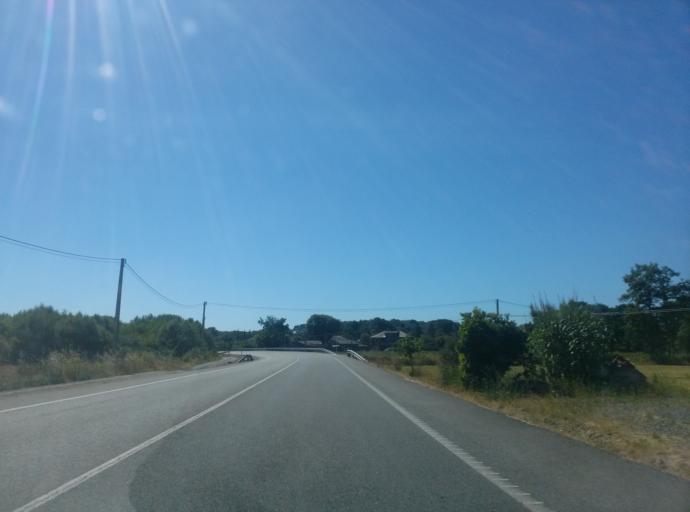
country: ES
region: Galicia
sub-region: Provincia de Lugo
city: Mos
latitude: 43.1229
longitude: -7.5532
